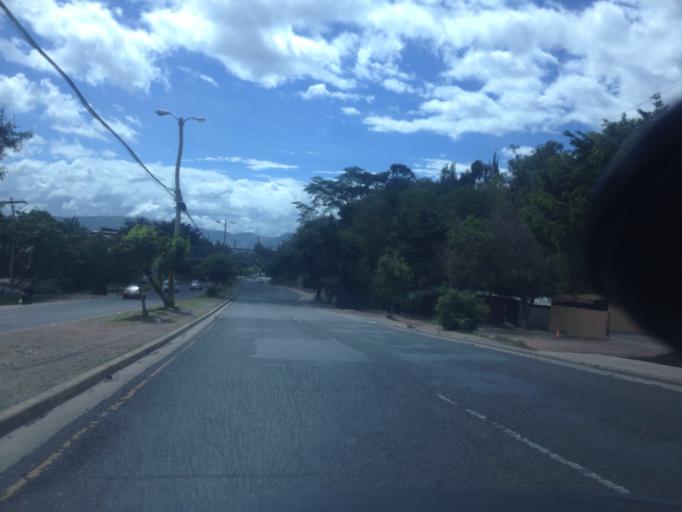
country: HN
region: Francisco Morazan
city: Tegucigalpa
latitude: 14.0707
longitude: -87.1759
